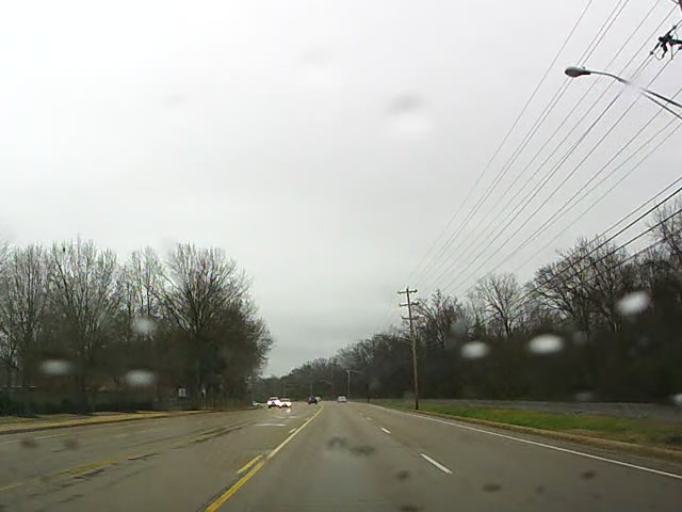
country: US
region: Tennessee
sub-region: Shelby County
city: Collierville
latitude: 35.0486
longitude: -89.7223
